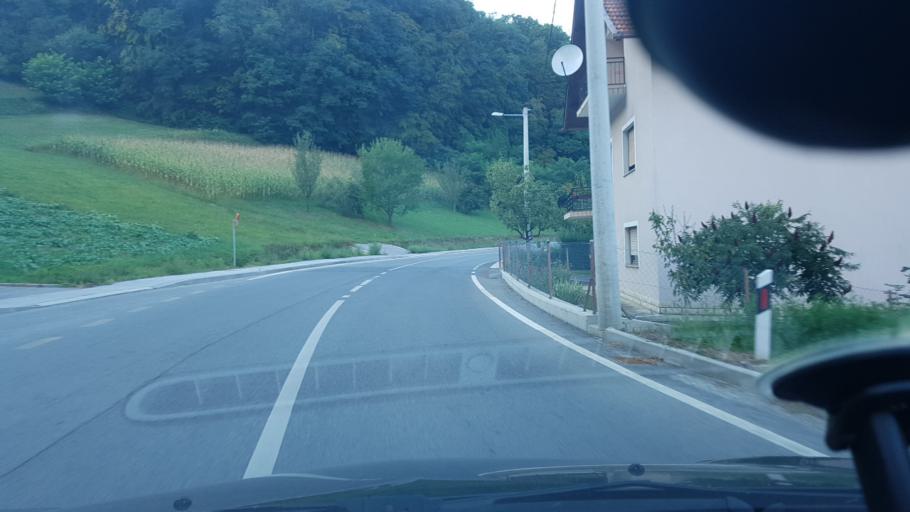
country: HR
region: Krapinsko-Zagorska
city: Pregrada
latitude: 46.1520
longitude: 15.7917
